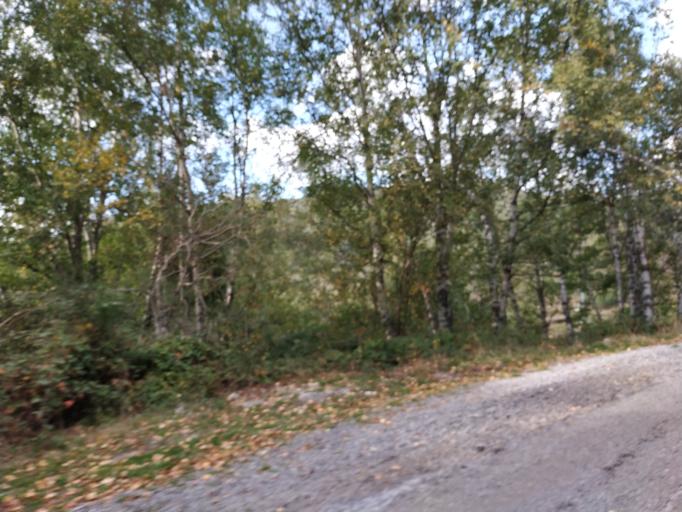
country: ES
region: Castille and Leon
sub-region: Provincia de Leon
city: Candin
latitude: 42.8654
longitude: -6.8498
